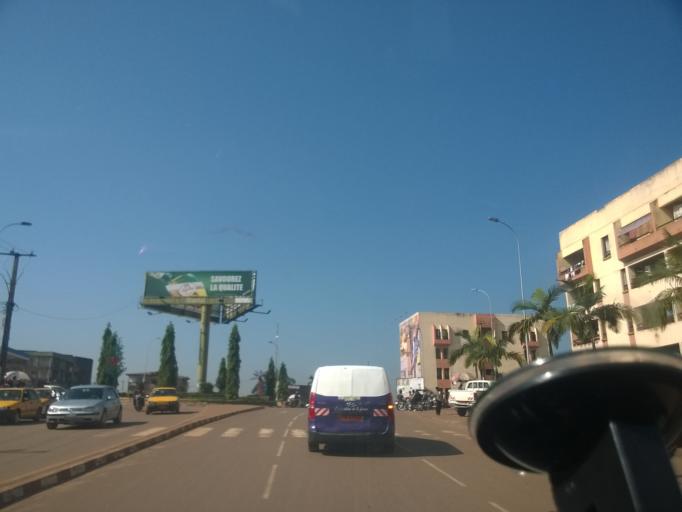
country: CM
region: Centre
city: Yaounde
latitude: 3.8366
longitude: 11.4845
